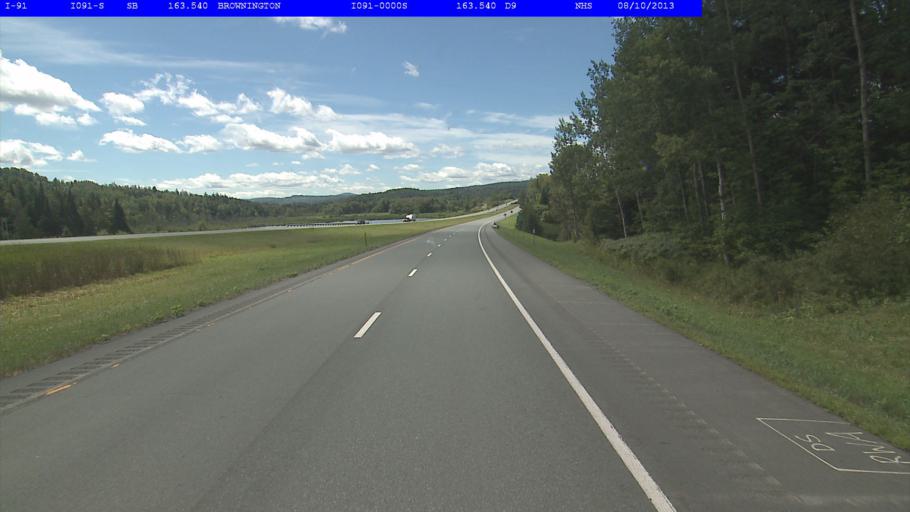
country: US
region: Vermont
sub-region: Orleans County
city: Newport
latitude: 44.8343
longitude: -72.1965
